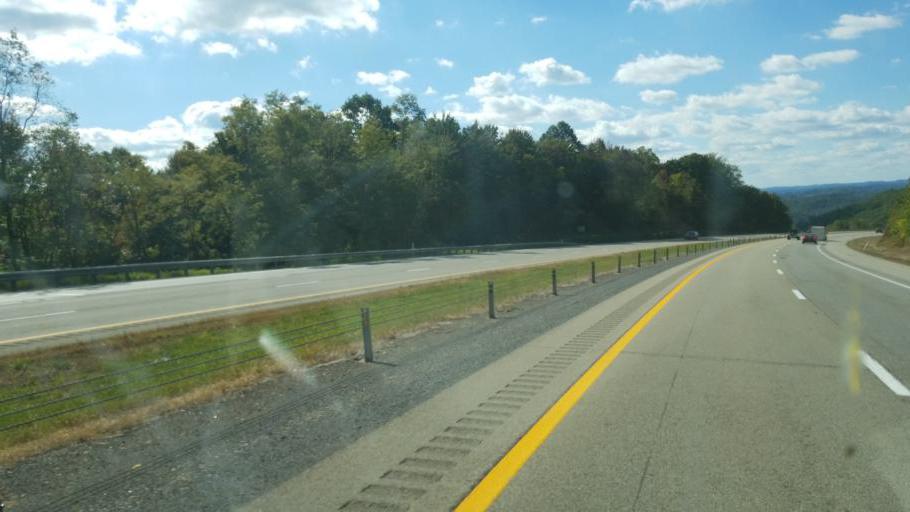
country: US
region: West Virginia
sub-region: Monongalia County
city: Cheat Lake
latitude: 39.6572
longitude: -79.8320
